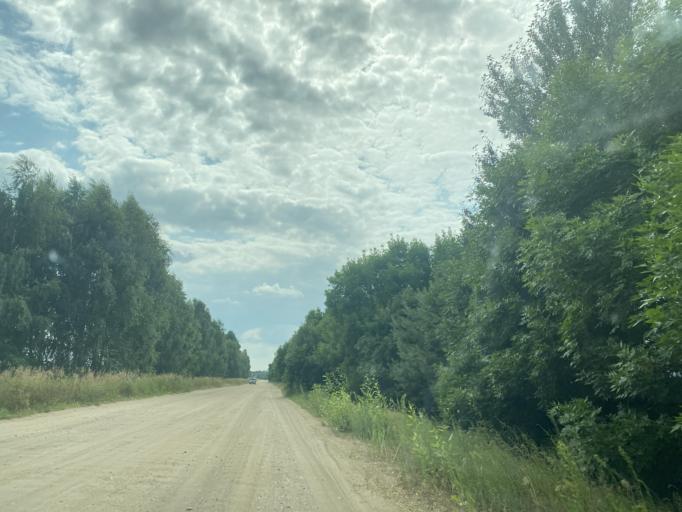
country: BY
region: Brest
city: Ivanava
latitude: 52.3614
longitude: 25.6360
